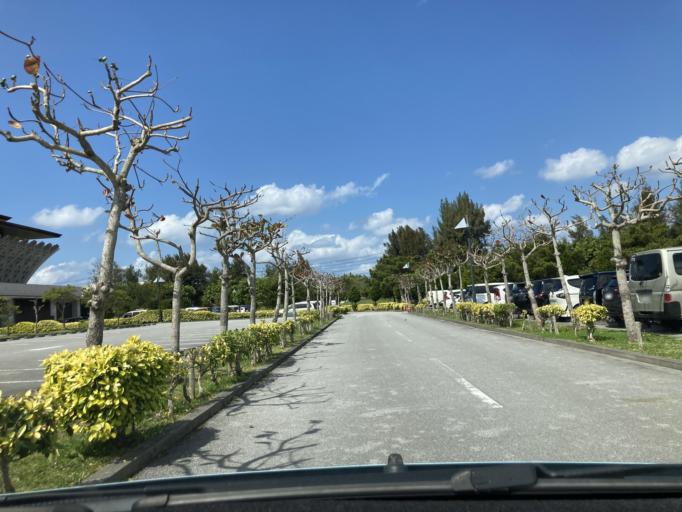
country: JP
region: Okinawa
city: Naha-shi
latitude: 26.2469
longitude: 127.6895
